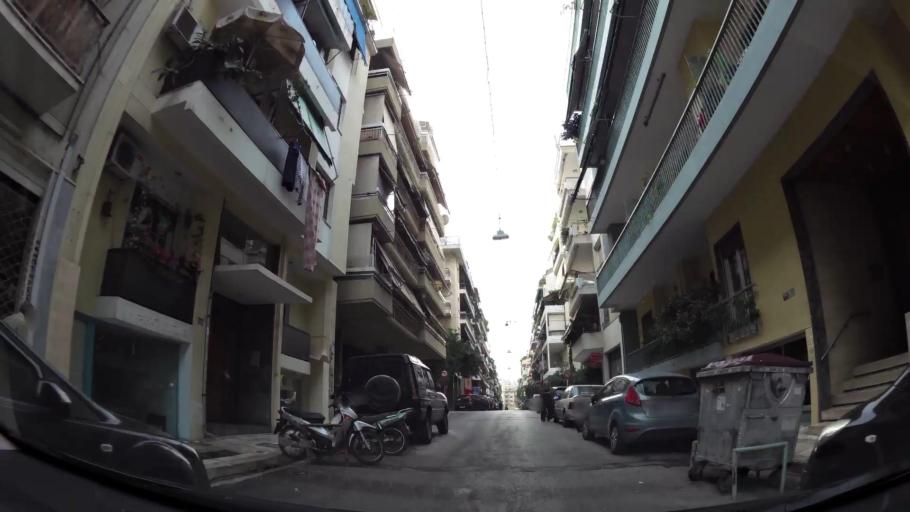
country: GR
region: Attica
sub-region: Nomarchia Athinas
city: Kipseli
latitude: 37.9921
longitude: 23.7445
